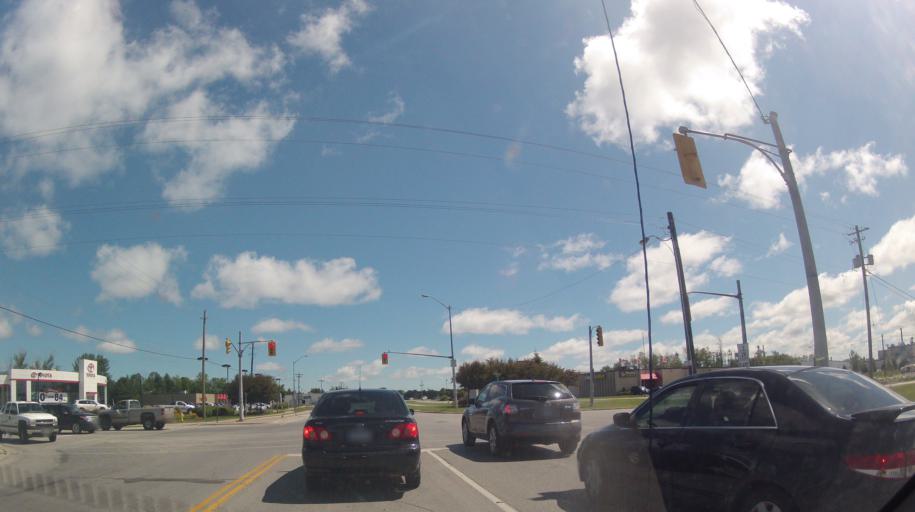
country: CA
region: Ontario
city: Collingwood
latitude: 44.4999
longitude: -80.1962
